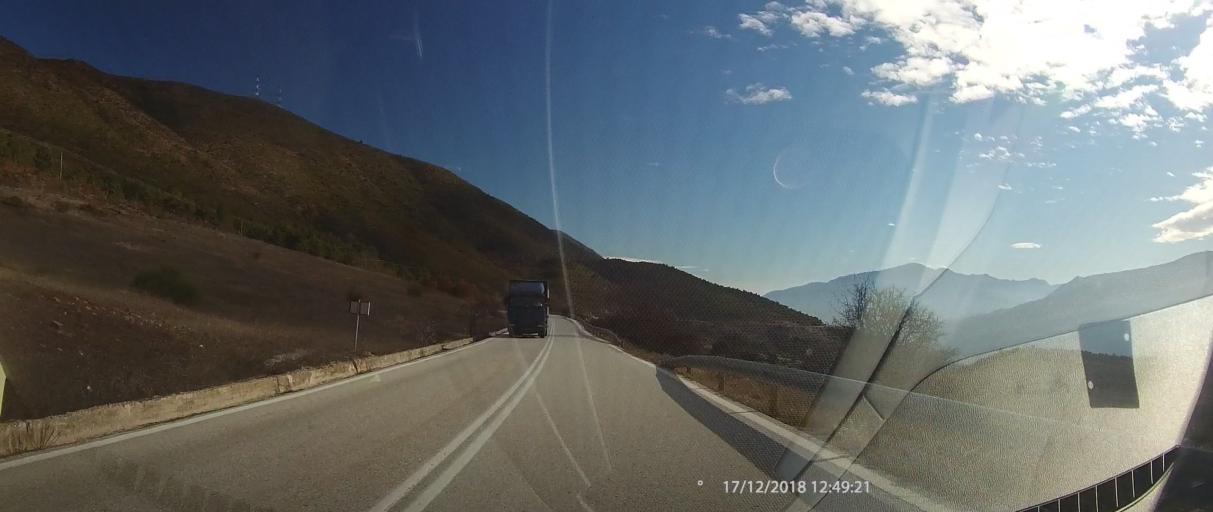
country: GR
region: Thessaly
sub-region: Trikala
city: Kastraki
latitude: 39.7790
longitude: 21.4438
